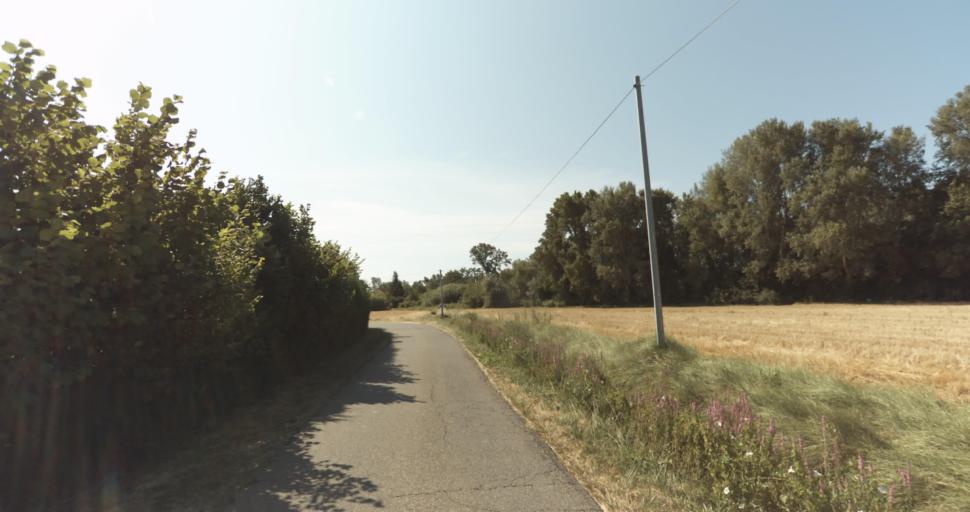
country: FR
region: Provence-Alpes-Cote d'Azur
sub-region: Departement du Vaucluse
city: Althen-des-Paluds
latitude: 44.0109
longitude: 4.9658
